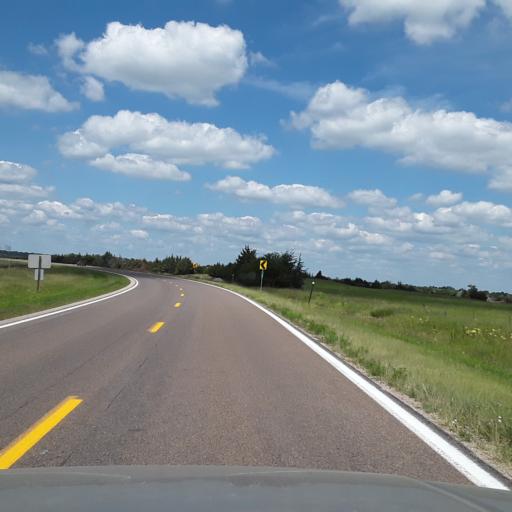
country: US
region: Nebraska
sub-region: Nance County
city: Genoa
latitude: 41.3949
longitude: -97.6941
